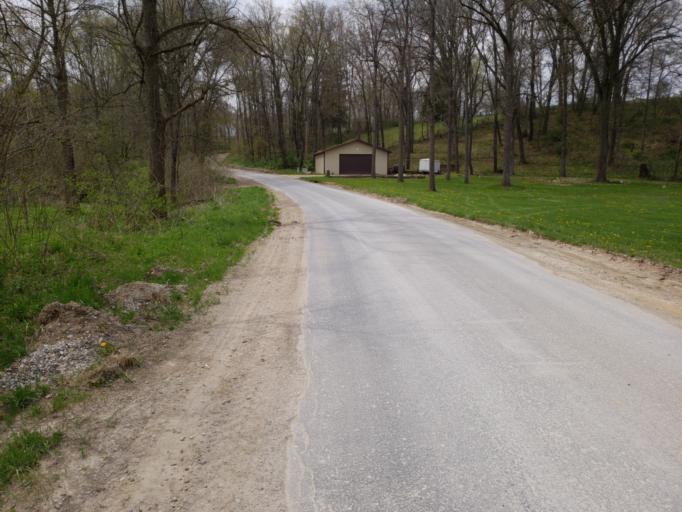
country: US
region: Ohio
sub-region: Tuscarawas County
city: Rockford
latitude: 40.4833
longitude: -81.2528
